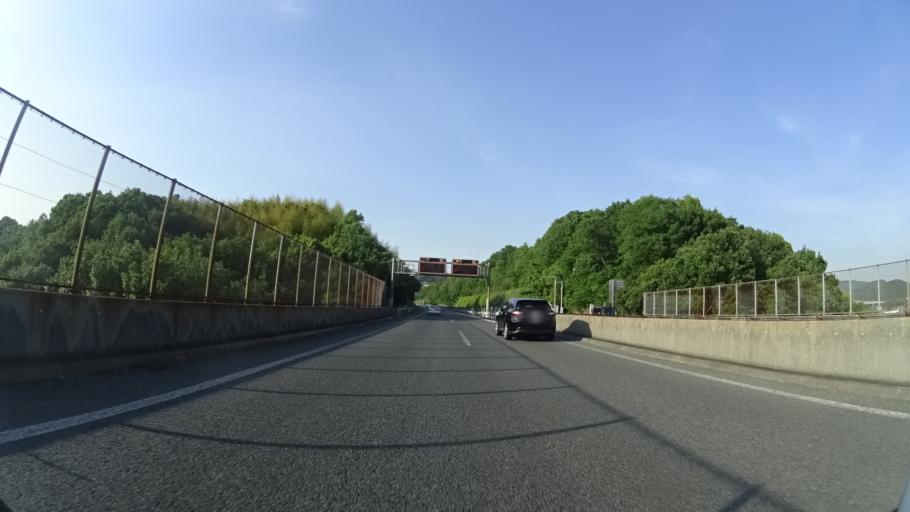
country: JP
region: Ehime
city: Kawanoecho
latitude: 33.9920
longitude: 133.5942
